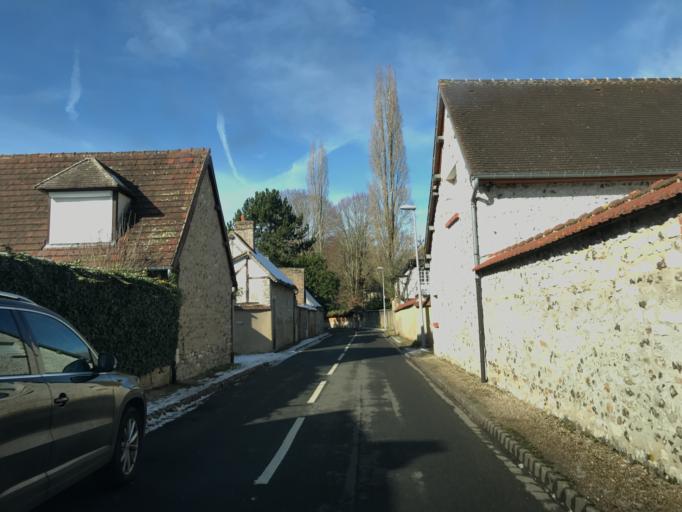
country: FR
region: Haute-Normandie
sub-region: Departement de l'Eure
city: Houlbec-Cocherel
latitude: 49.0685
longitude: 1.2903
